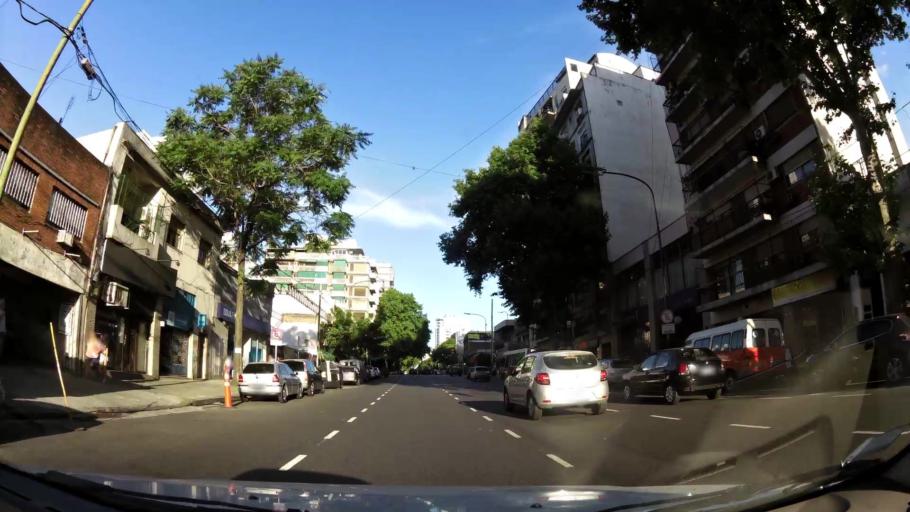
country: AR
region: Buenos Aires F.D.
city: Colegiales
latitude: -34.6088
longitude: -58.4410
